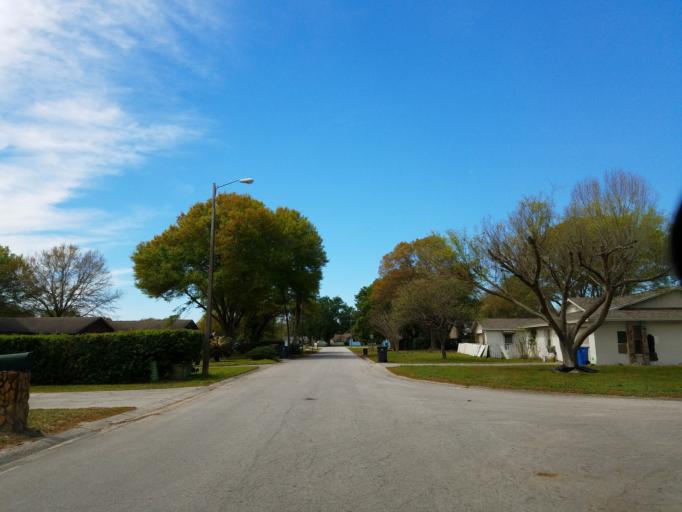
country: US
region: Florida
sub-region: Hillsborough County
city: Thonotosassa
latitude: 28.0658
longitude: -82.3074
